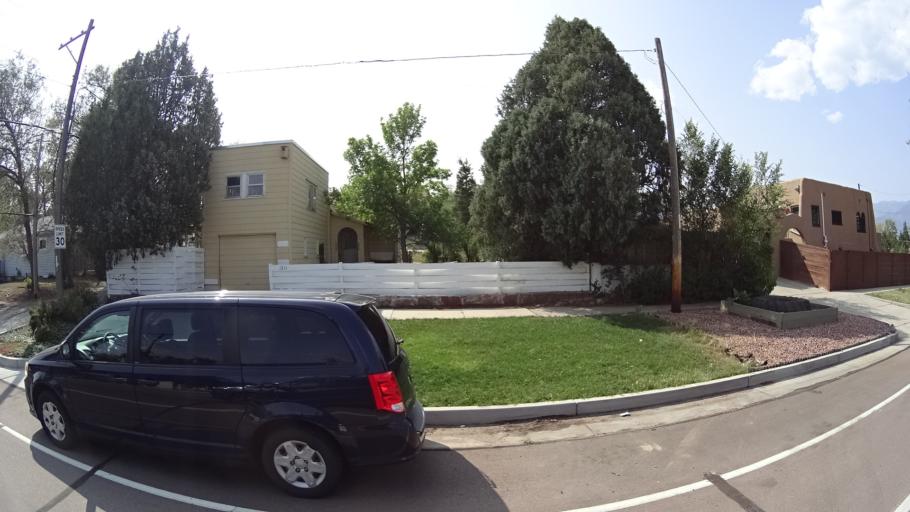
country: US
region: Colorado
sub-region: El Paso County
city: Colorado Springs
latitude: 38.8360
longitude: -104.8032
